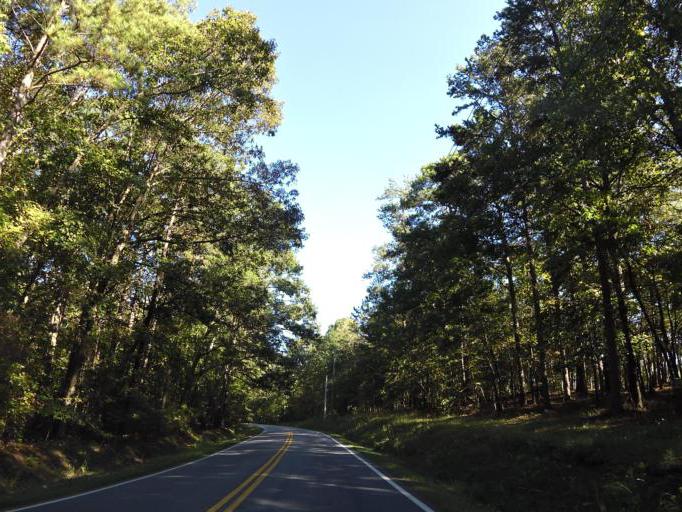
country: US
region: Georgia
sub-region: Bartow County
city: Emerson
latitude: 34.1342
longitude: -84.6949
